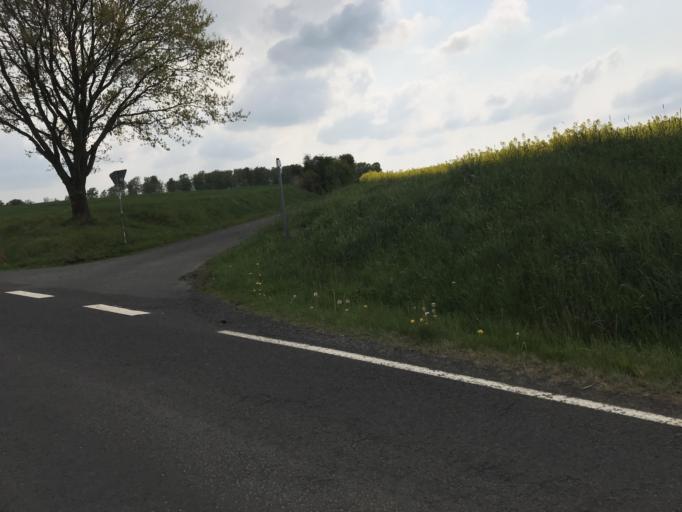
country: DE
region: Hesse
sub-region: Regierungsbezirk Giessen
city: Laubach
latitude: 50.5307
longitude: 8.9936
